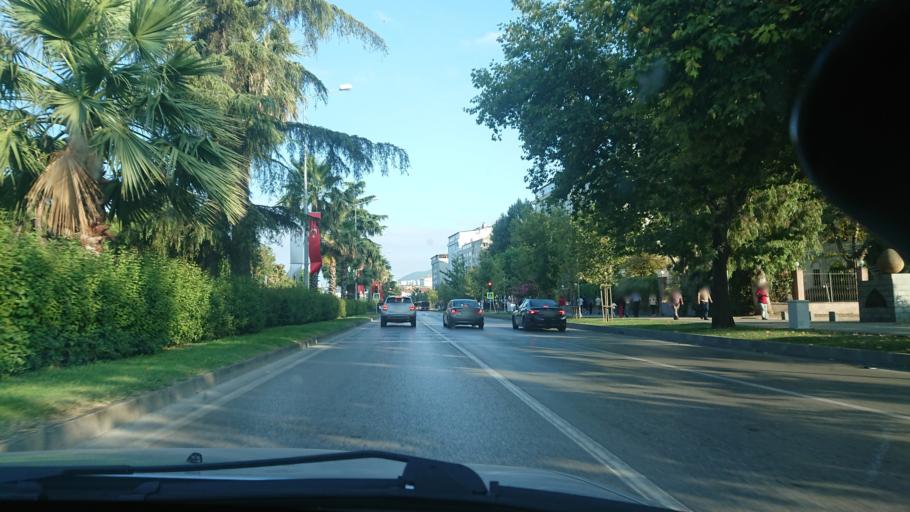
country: TR
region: Samsun
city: Samsun
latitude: 41.2893
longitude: 36.3372
